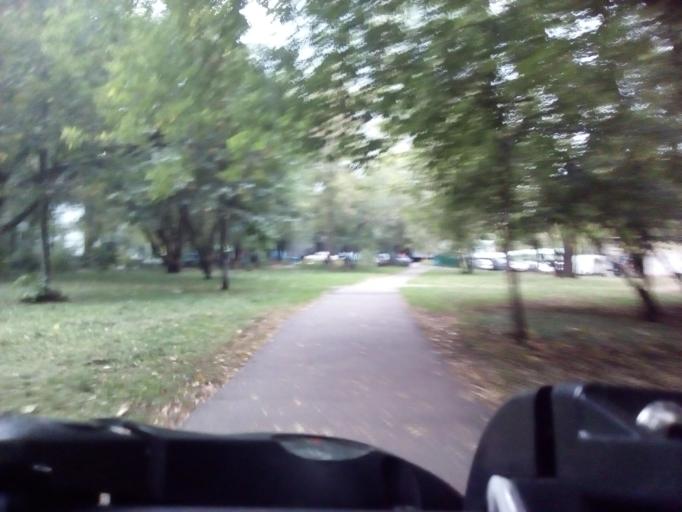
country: RU
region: Moscow
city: Sviblovo
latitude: 55.8546
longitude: 37.6406
